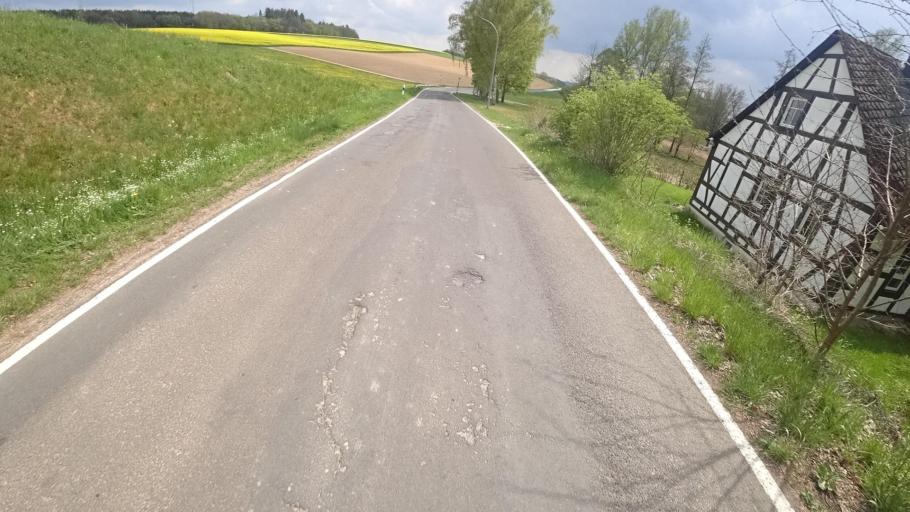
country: DE
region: Rheinland-Pfalz
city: Klosterkumbd
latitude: 50.0250
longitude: 7.5368
